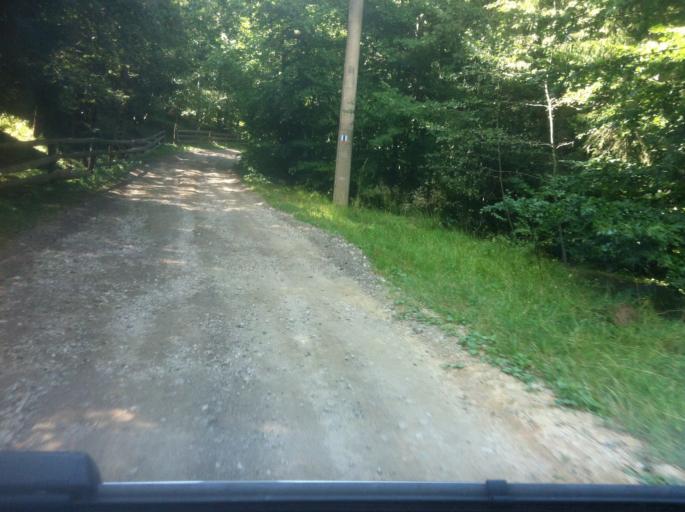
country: RO
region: Hunedoara
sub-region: Comuna Rau de Mori
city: Rau de Mori
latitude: 45.4330
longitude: 22.8947
